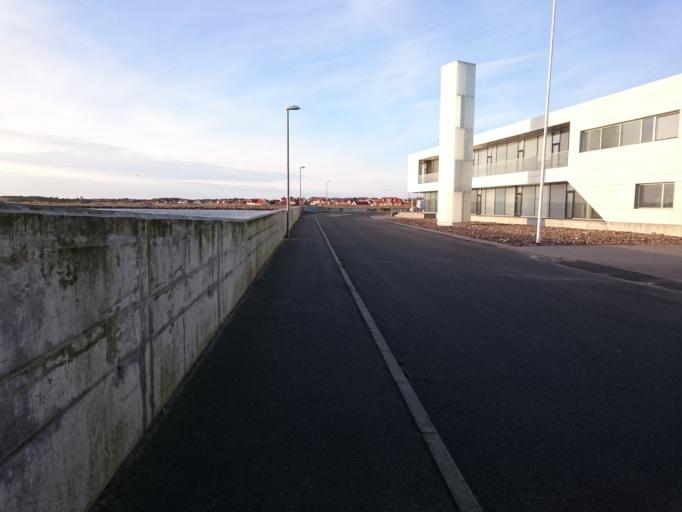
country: DK
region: North Denmark
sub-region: Frederikshavn Kommune
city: Skagen
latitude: 57.7135
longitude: 10.5804
